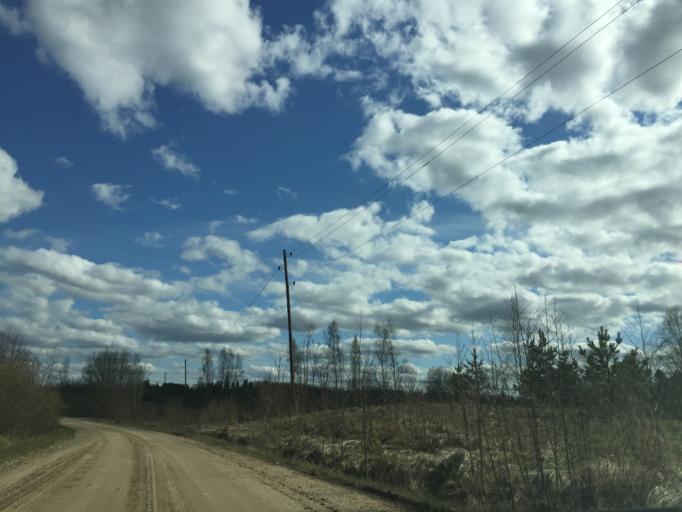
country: LV
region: Rezekne
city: Rezekne
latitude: 56.6482
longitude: 27.2870
